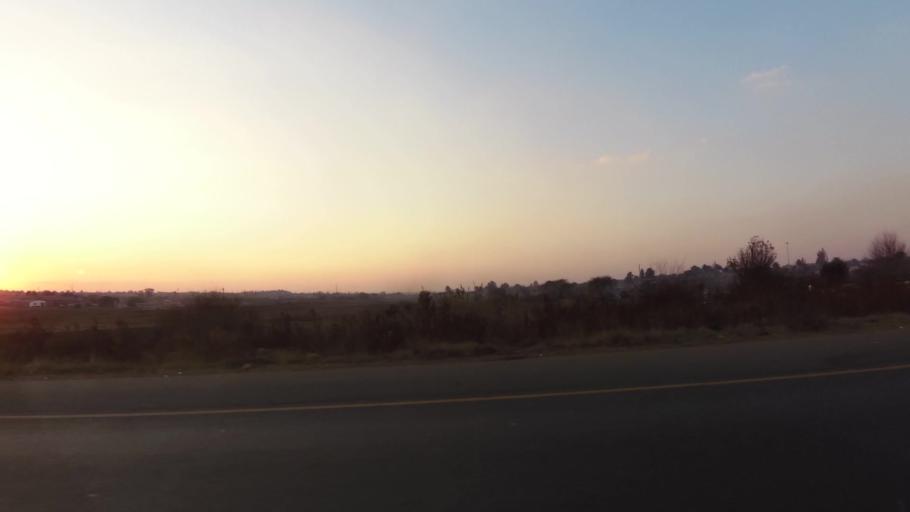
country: ZA
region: Gauteng
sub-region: City of Johannesburg Metropolitan Municipality
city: Soweto
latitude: -26.2896
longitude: 27.8866
